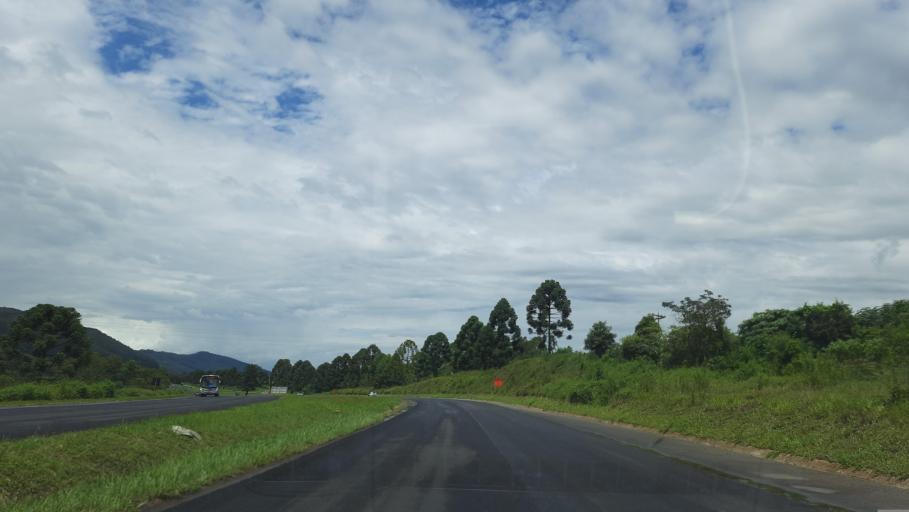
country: BR
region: Minas Gerais
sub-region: Pocos De Caldas
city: Pocos de Caldas
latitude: -21.8217
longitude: -46.6660
